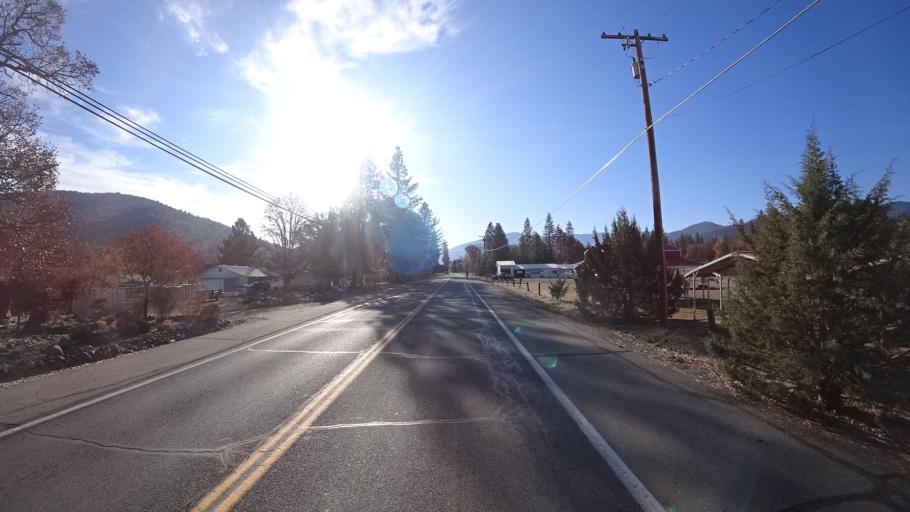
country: US
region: California
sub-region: Siskiyou County
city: Yreka
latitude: 41.6899
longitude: -122.6365
